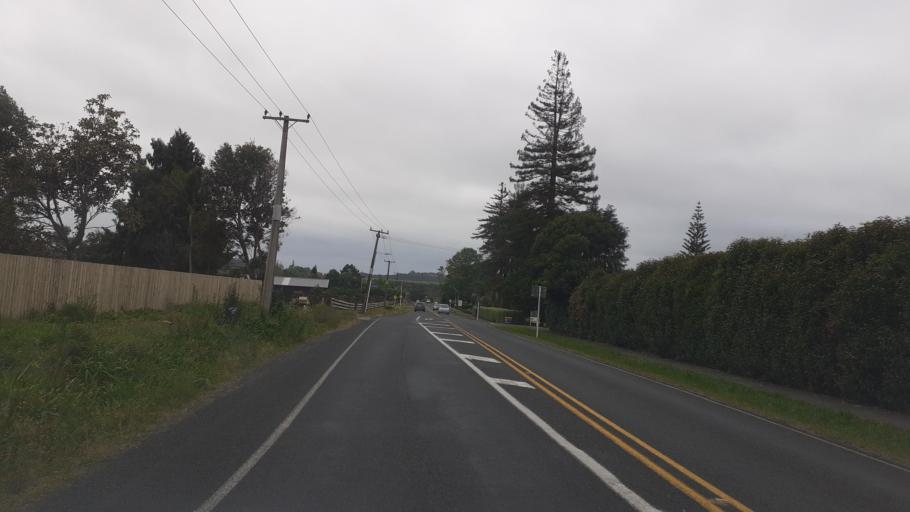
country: NZ
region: Northland
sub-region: Far North District
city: Kerikeri
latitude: -35.2097
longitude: 173.9632
